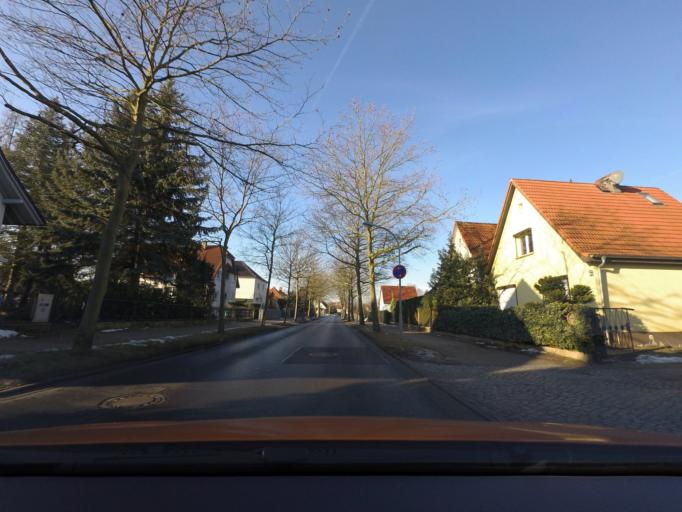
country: DE
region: Brandenburg
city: Falkensee
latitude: 52.5529
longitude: 13.0899
